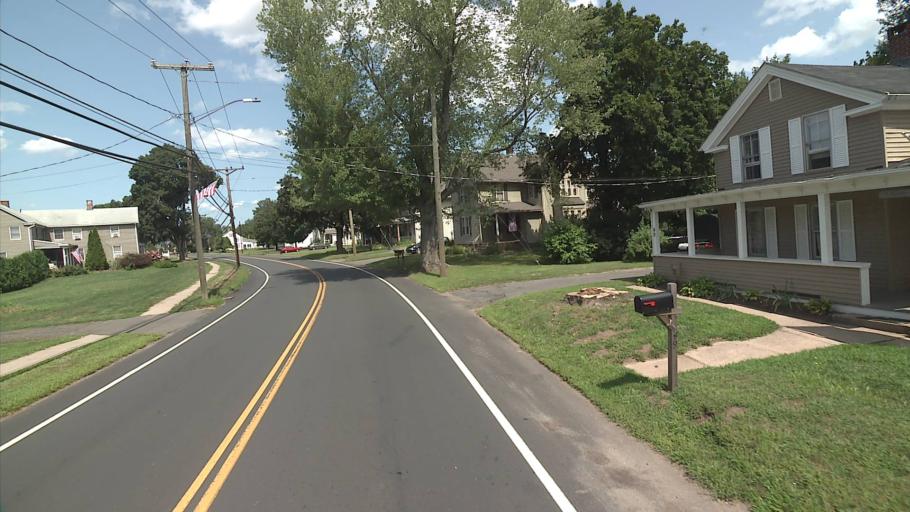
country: US
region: Connecticut
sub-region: Hartford County
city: Broad Brook
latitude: 41.9214
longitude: -72.5447
